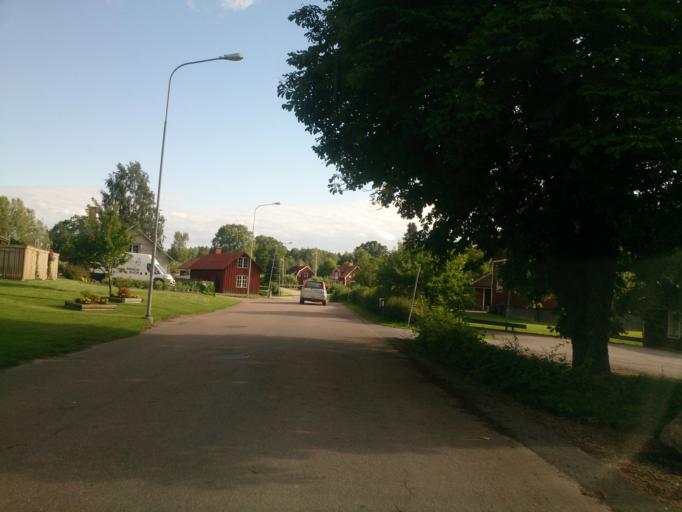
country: SE
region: OEstergoetland
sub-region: Atvidabergs Kommun
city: Atvidaberg
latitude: 58.3340
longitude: 16.0230
